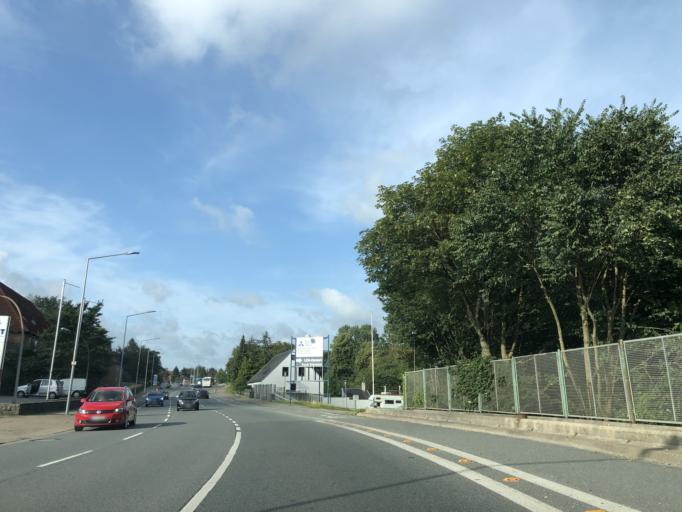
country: DE
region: Schleswig-Holstein
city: Flensburg
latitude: 54.7773
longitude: 9.4295
